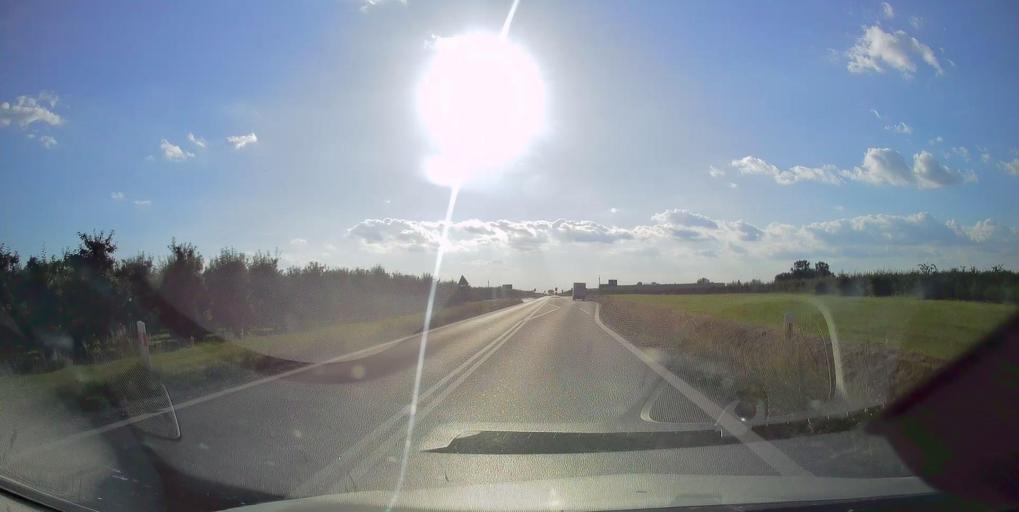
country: PL
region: Lodz Voivodeship
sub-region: Powiat rawski
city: Sadkowice
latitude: 51.8056
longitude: 20.5793
